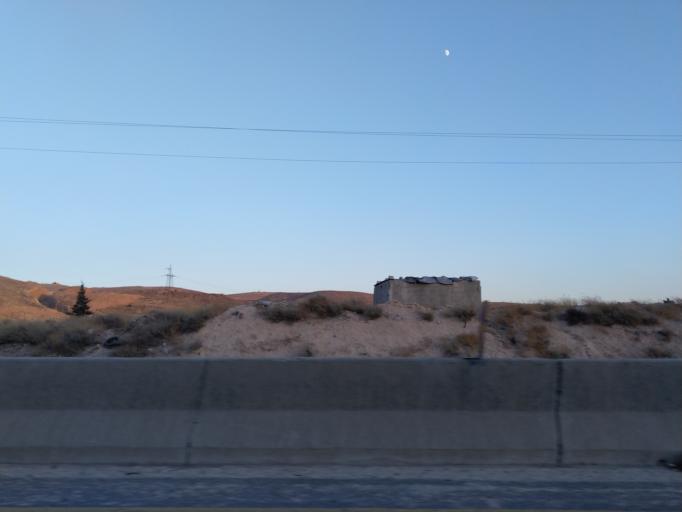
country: SY
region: Rif-dimashq
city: At Tall
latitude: 33.5865
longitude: 36.3062
